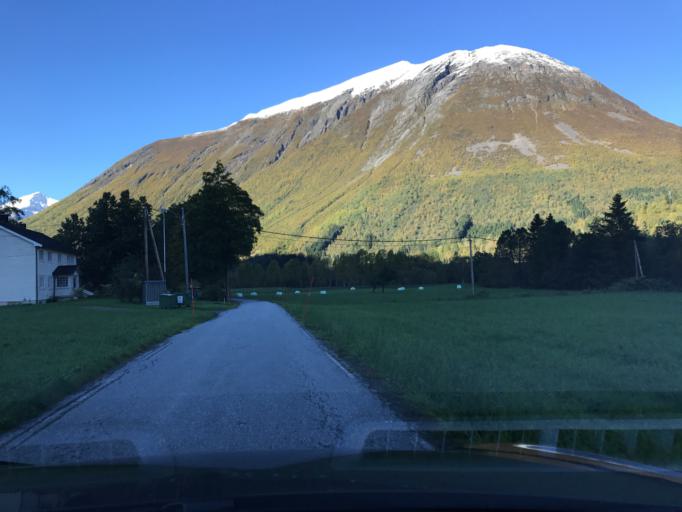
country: NO
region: More og Romsdal
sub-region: Norddal
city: Valldal
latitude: 62.3304
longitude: 7.3590
